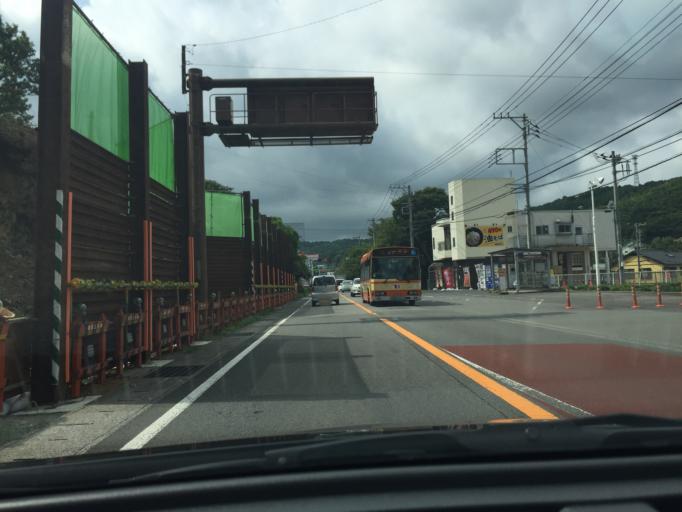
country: JP
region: Shizuoka
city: Ito
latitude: 34.9437
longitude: 139.1177
